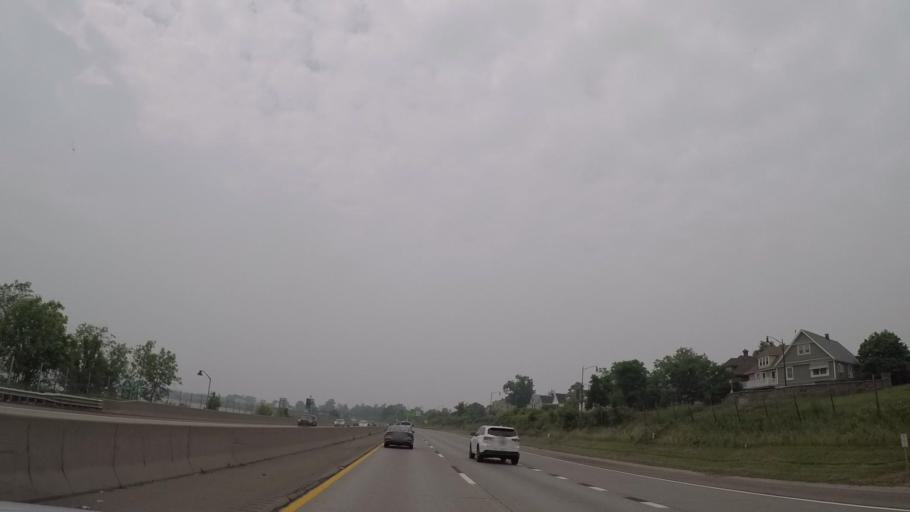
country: US
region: New York
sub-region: Erie County
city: Kenmore
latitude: 42.9494
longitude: -78.9091
